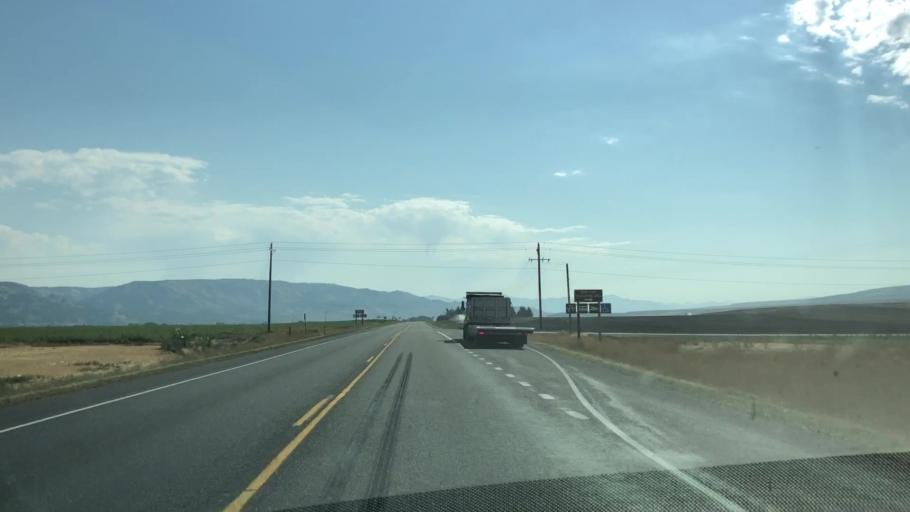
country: US
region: Idaho
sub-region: Jefferson County
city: Rigby
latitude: 43.6133
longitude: -111.7497
